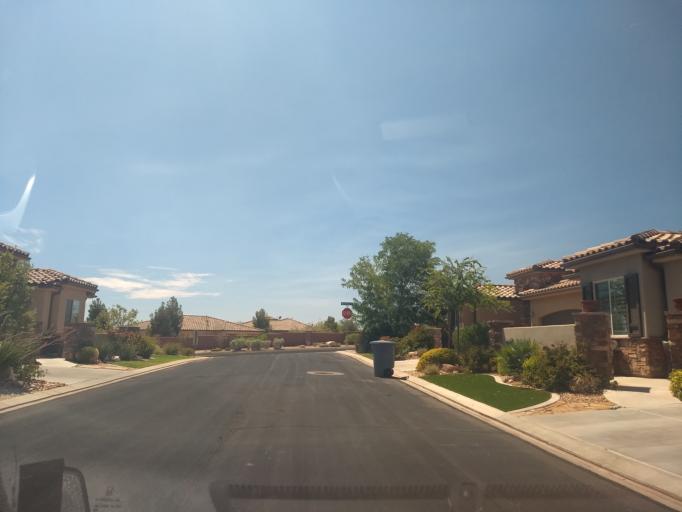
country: US
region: Utah
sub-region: Washington County
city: Washington
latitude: 37.1407
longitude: -113.4824
